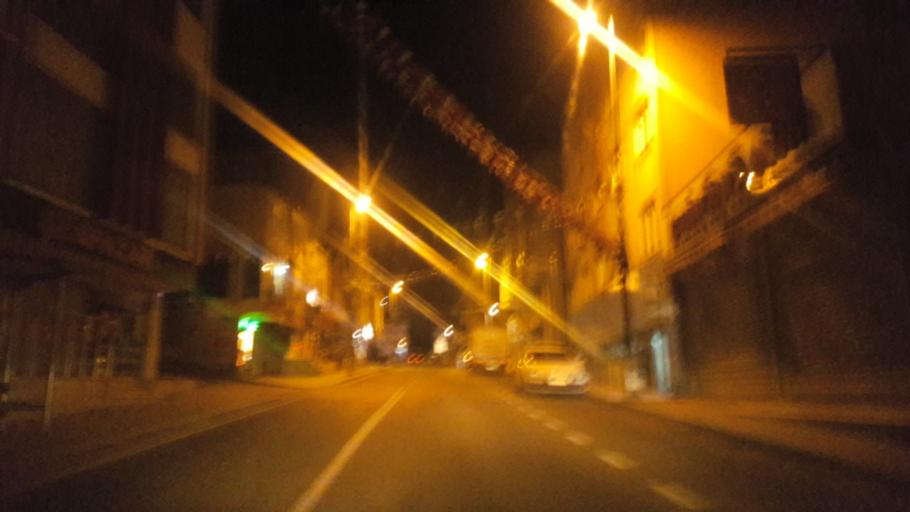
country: TR
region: Kocaeli
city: Tavsancil
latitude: 40.7858
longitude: 29.5395
